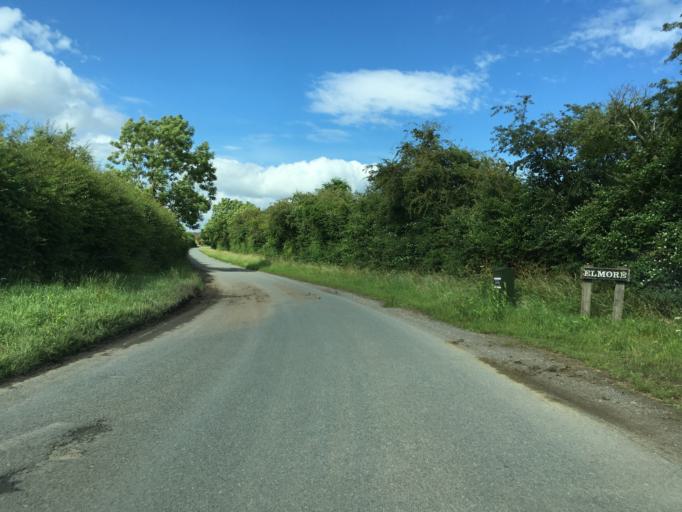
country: GB
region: England
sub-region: Gloucestershire
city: Stonehouse
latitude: 51.8291
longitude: -2.3431
